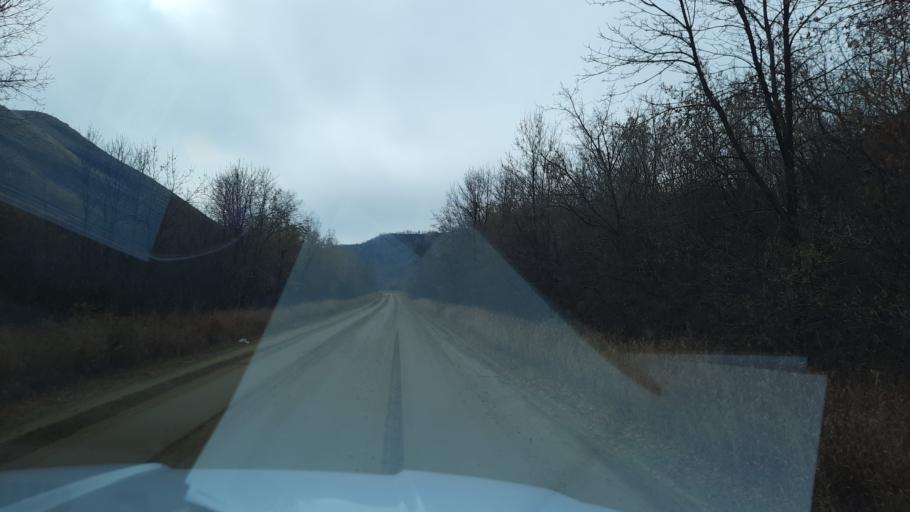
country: CA
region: Saskatchewan
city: White City
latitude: 50.7778
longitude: -104.1347
